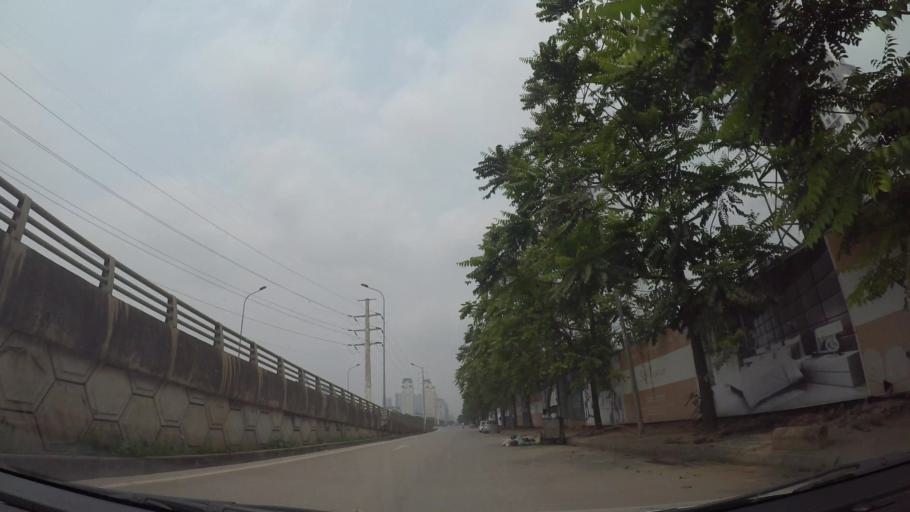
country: VN
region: Ha Noi
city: Cau Dien
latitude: 21.0070
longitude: 105.7677
